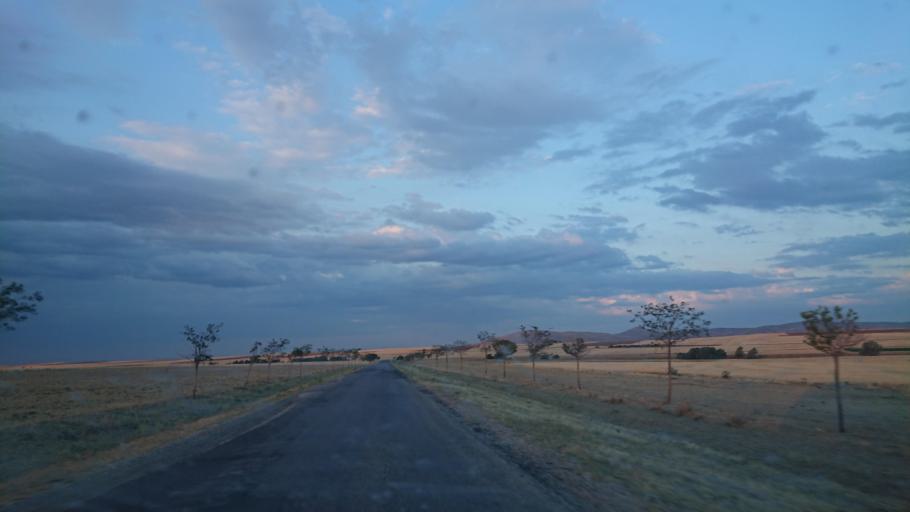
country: TR
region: Aksaray
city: Balci
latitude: 38.8264
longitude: 34.1199
